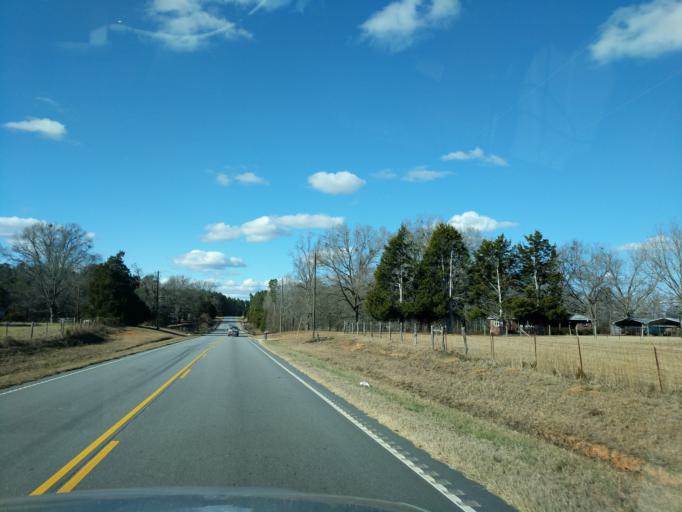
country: US
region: South Carolina
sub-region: Greenwood County
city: Ninety Six
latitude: 34.0920
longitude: -82.0955
